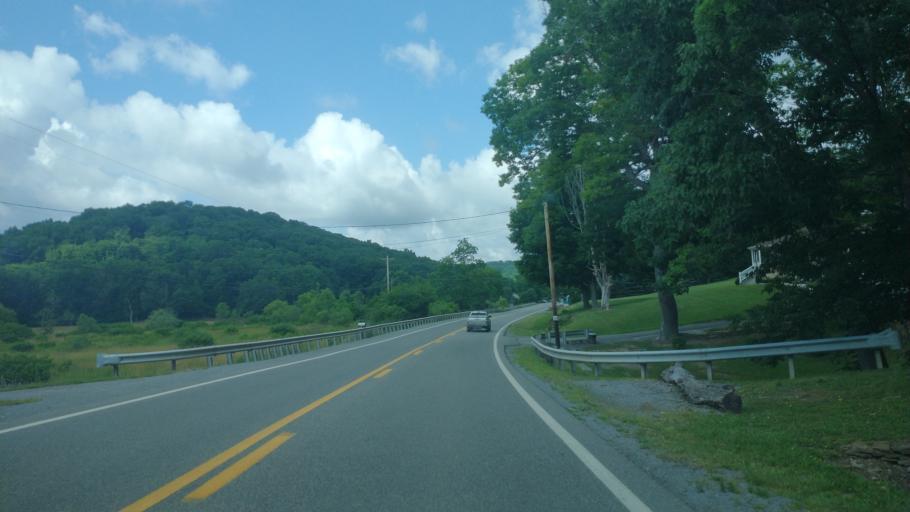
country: US
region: West Virginia
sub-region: Mercer County
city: Princeton
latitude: 37.3351
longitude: -81.1720
